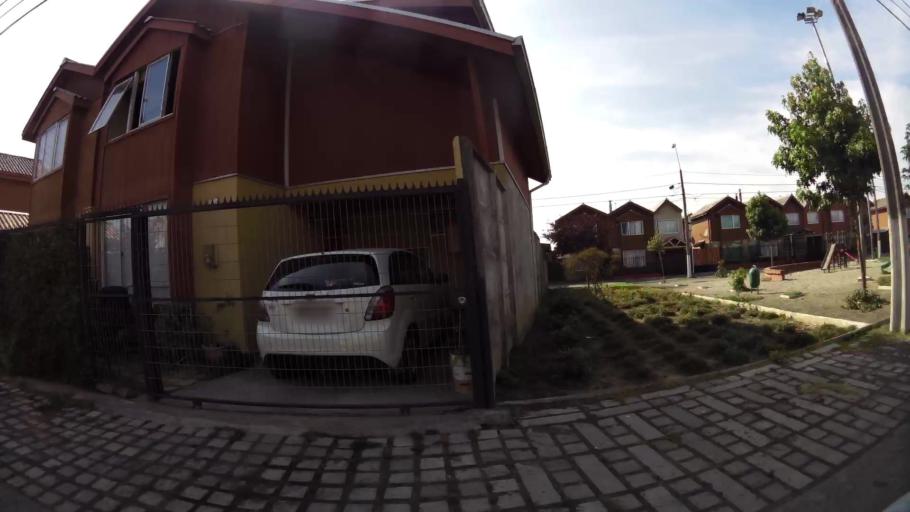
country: CL
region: Biobio
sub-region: Provincia de Concepcion
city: Talcahuano
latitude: -36.7923
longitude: -73.1152
